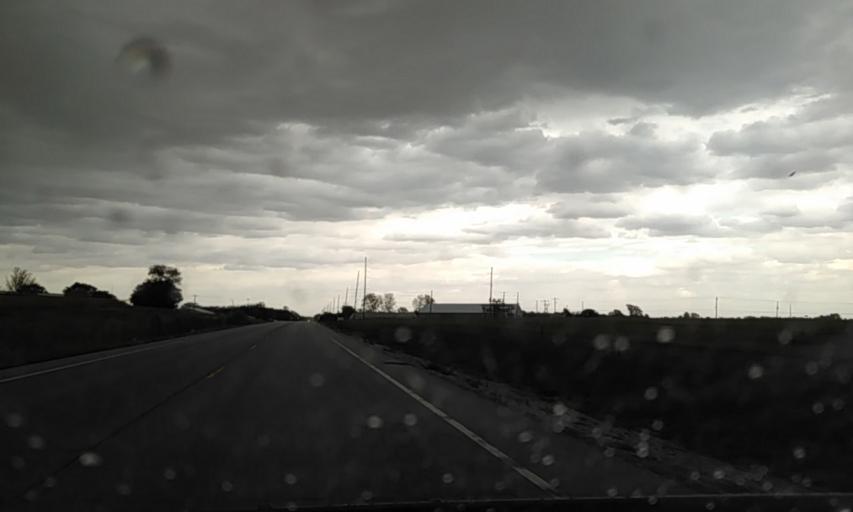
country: US
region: Illinois
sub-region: Bond County
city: Greenville
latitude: 38.8722
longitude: -89.4079
